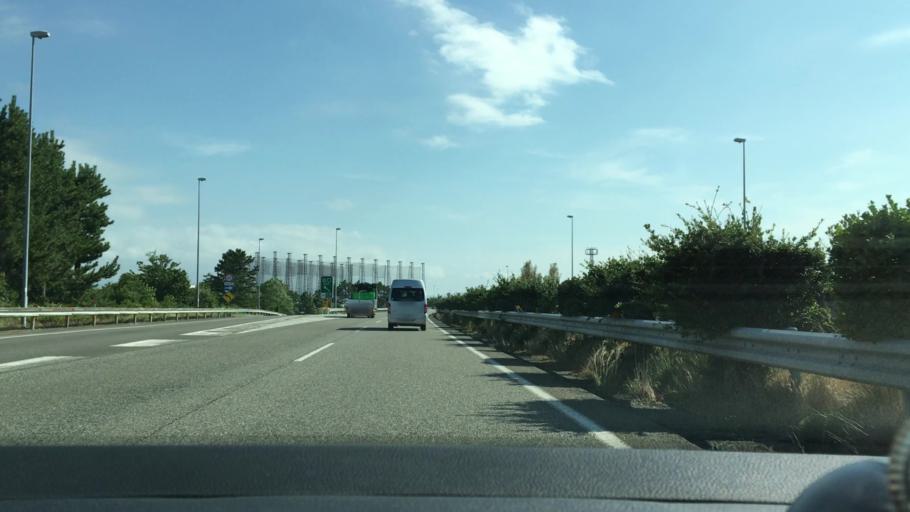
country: JP
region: Ishikawa
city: Komatsu
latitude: 36.4249
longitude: 136.4314
